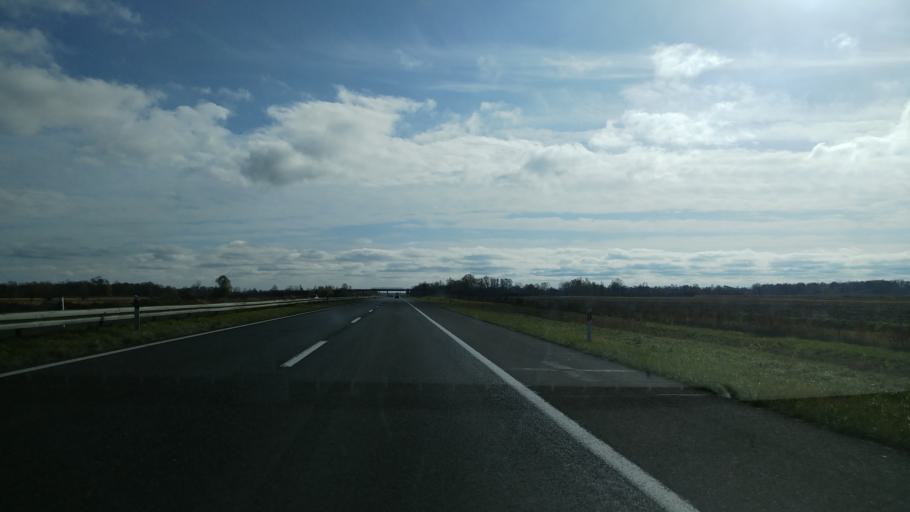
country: HR
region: Zagrebacka
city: Lupoglav
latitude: 45.7217
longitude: 16.3445
